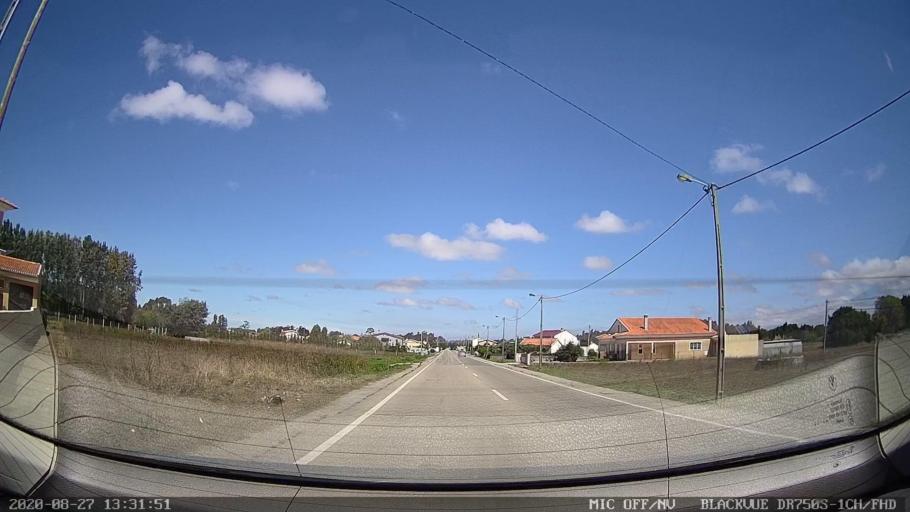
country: PT
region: Aveiro
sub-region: Vagos
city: Vagos
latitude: 40.4927
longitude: -8.6852
